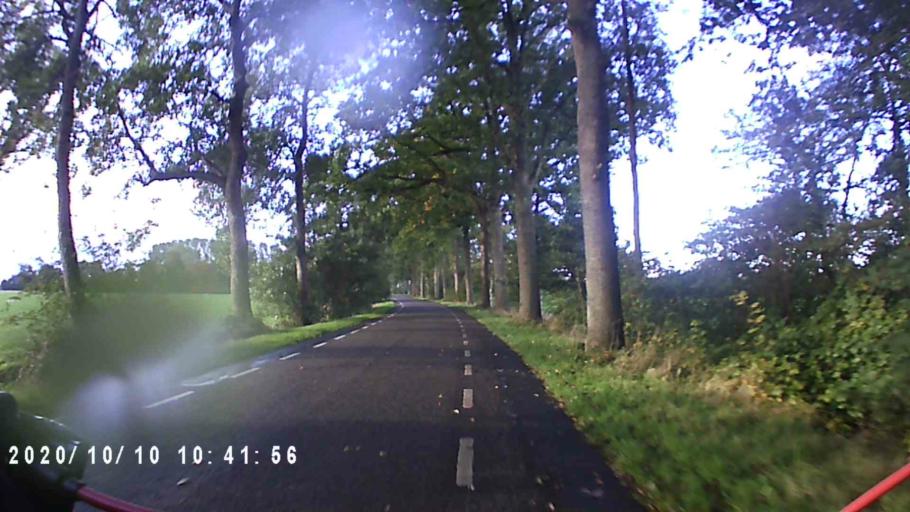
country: NL
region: Groningen
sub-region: Gemeente Grootegast
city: Grootegast
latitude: 53.1755
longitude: 6.2756
